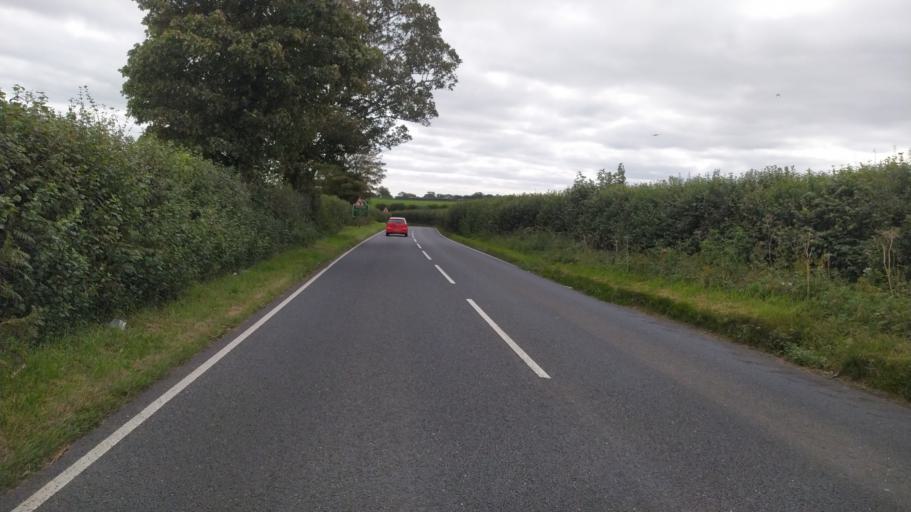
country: GB
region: England
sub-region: Somerset
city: Wincanton
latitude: 51.0614
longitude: -2.3493
